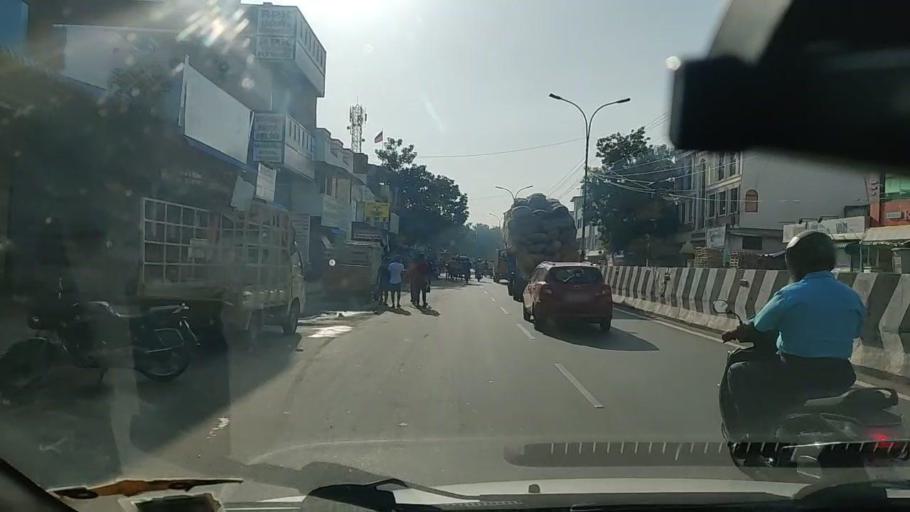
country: IN
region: Tamil Nadu
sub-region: Thiruvallur
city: Chinnasekkadu
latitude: 13.1220
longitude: 80.2517
